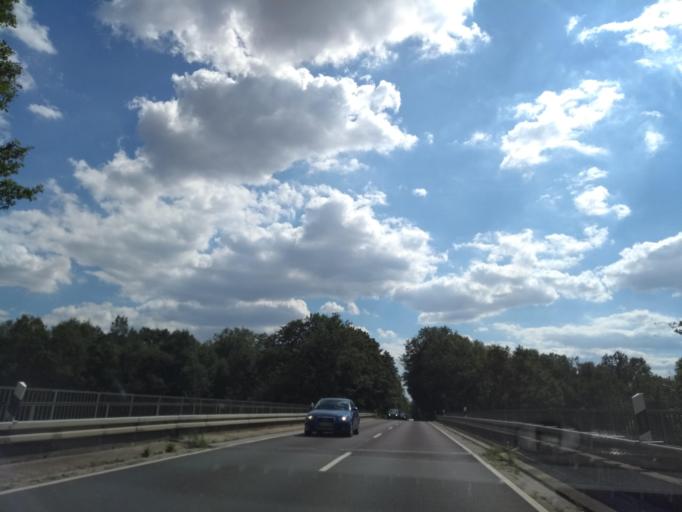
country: DE
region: Lower Saxony
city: Haste
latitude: 52.3922
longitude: 9.4000
